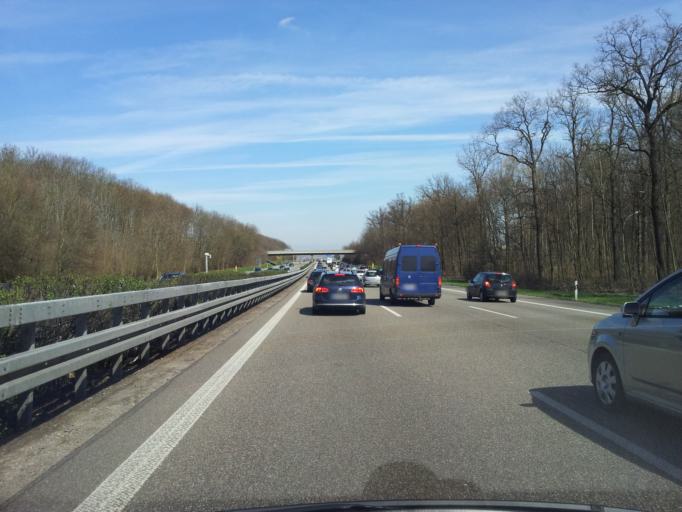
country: DE
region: Baden-Wuerttemberg
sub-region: Regierungsbezirk Stuttgart
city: Asperg
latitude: 48.8945
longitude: 9.1506
